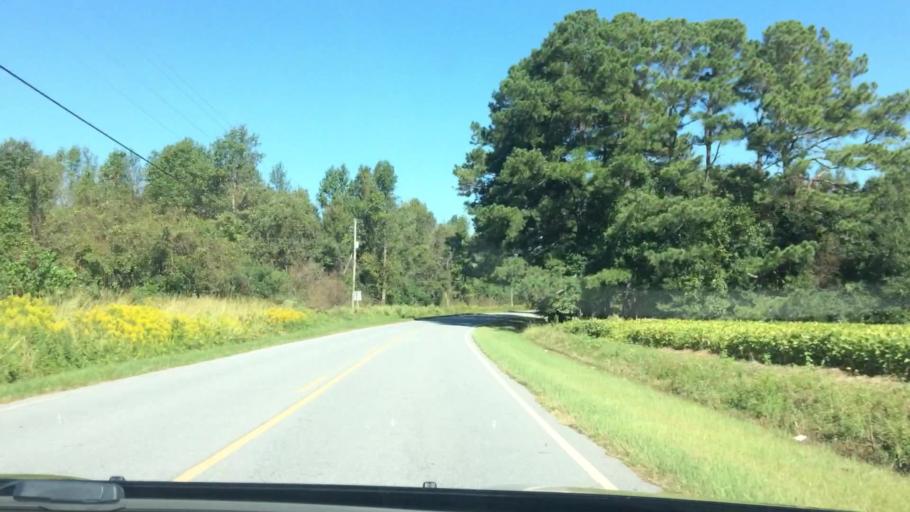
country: US
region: North Carolina
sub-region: Pitt County
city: Winterville
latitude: 35.5221
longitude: -77.4426
